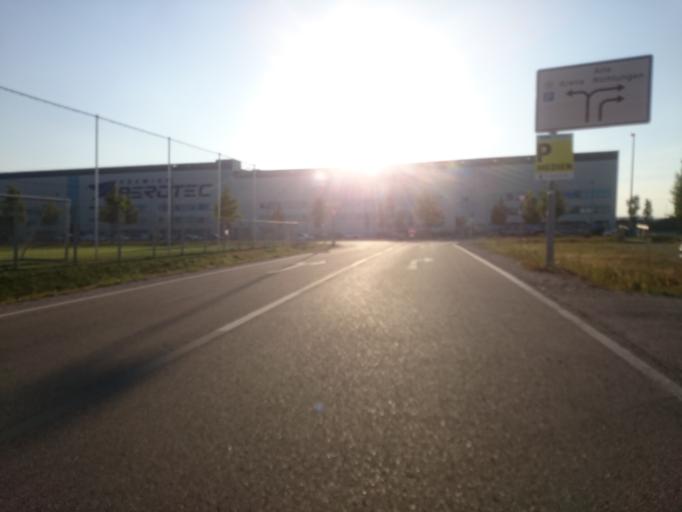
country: DE
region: Bavaria
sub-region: Swabia
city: Konigsbrunn
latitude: 48.3237
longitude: 10.8807
